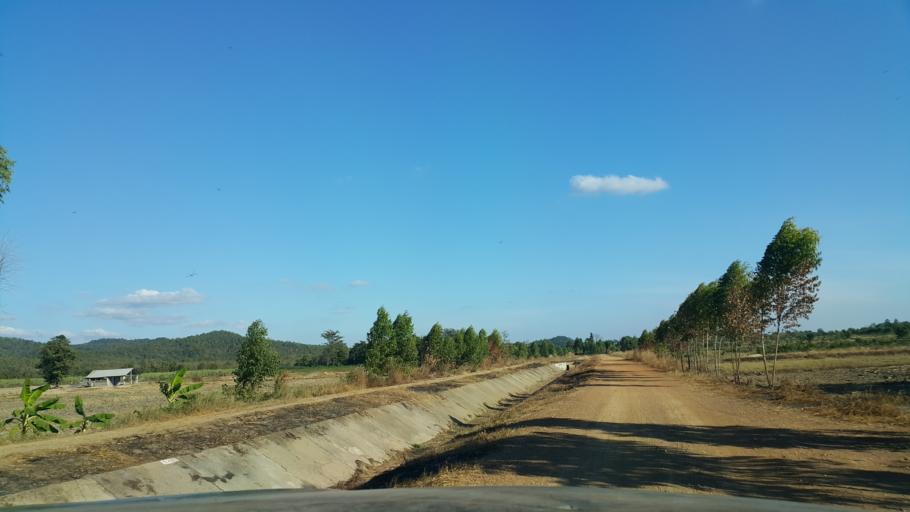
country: TH
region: Sukhothai
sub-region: Amphoe Si Satchanalai
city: Si Satchanalai
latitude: 17.4805
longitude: 99.6532
